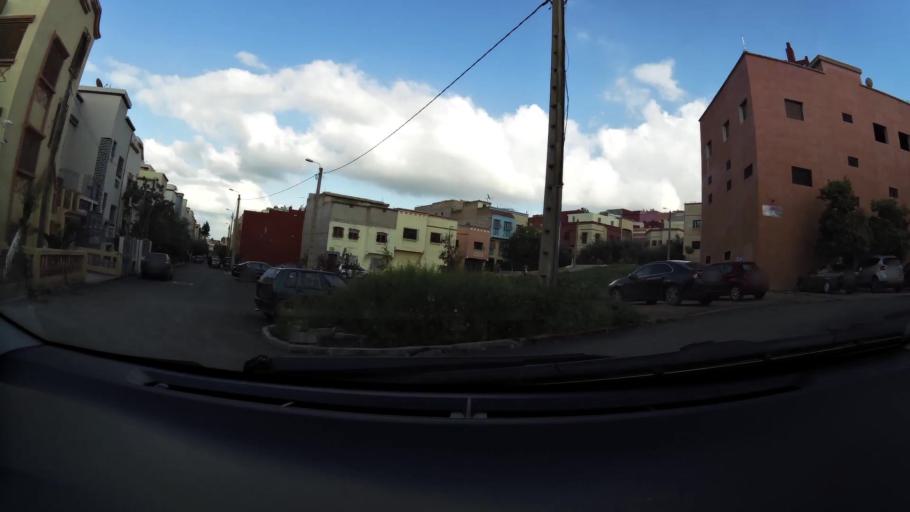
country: MA
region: Chaouia-Ouardigha
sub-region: Settat Province
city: Settat
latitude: 33.0060
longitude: -7.6369
